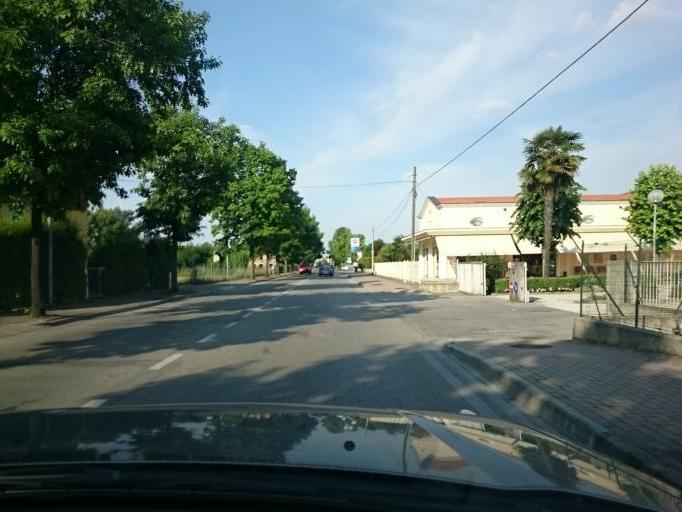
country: IT
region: Veneto
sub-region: Provincia di Padova
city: Montegrotto Terme
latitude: 45.3395
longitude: 11.7927
